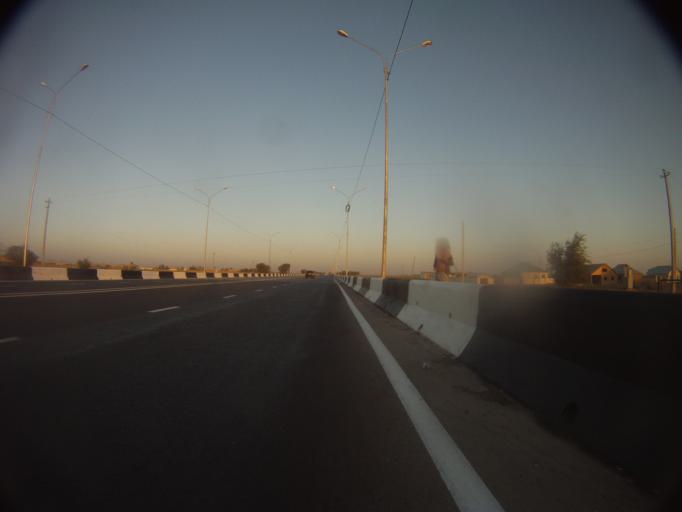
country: KZ
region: Ongtustik Qazaqstan
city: Turkestan
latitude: 43.2544
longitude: 68.3889
